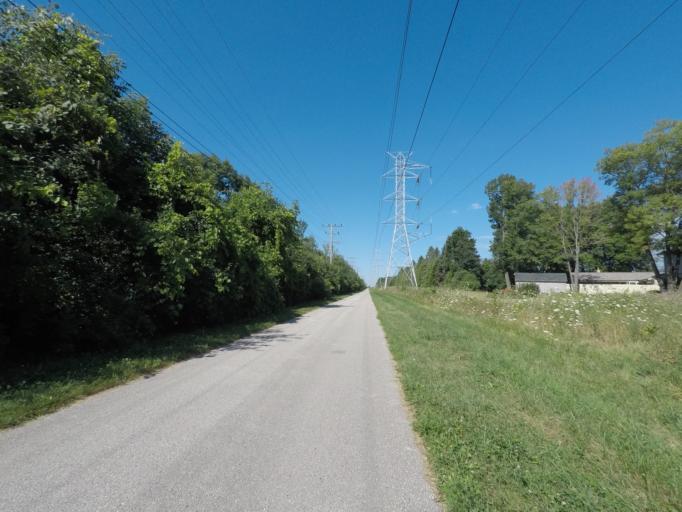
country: US
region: Wisconsin
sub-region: Waukesha County
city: Elm Grove
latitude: 43.0102
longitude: -88.0944
